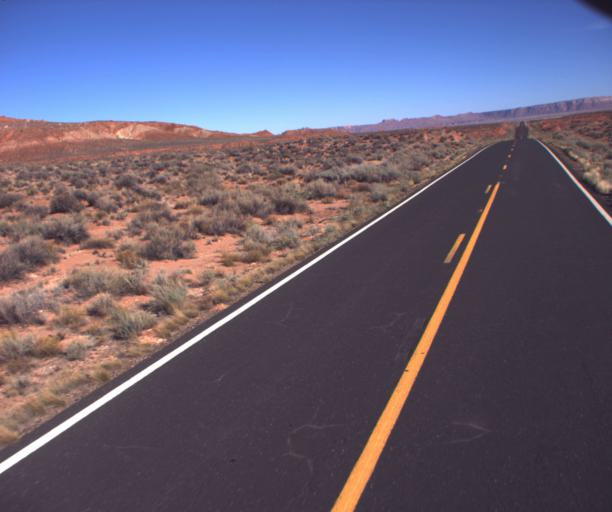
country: US
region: Arizona
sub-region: Coconino County
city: Page
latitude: 36.6886
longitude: -111.8742
